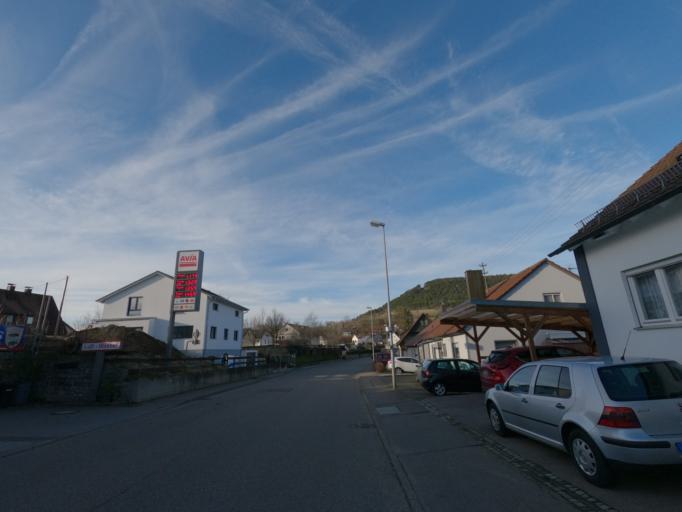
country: DE
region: Baden-Wuerttemberg
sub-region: Regierungsbezirk Stuttgart
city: Waldstetten
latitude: 48.7328
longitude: 9.8135
